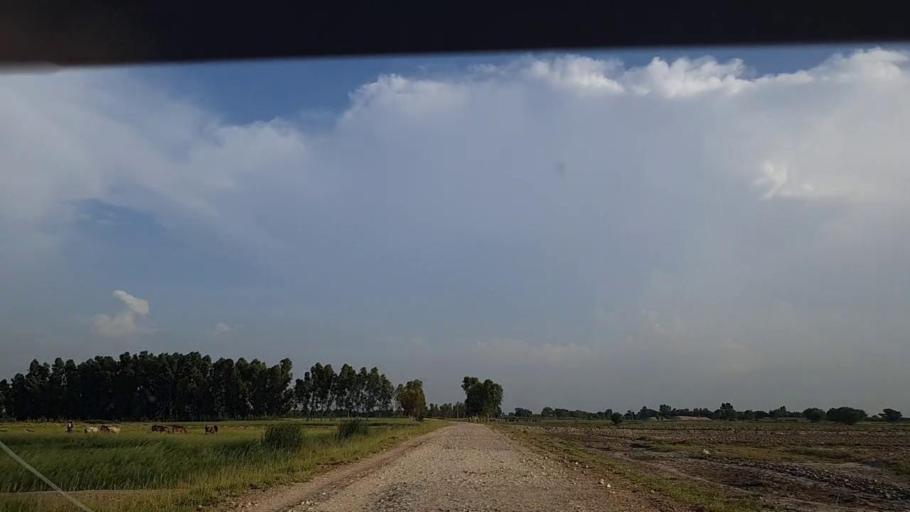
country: PK
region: Sindh
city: Khanpur
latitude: 27.8144
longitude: 69.3361
